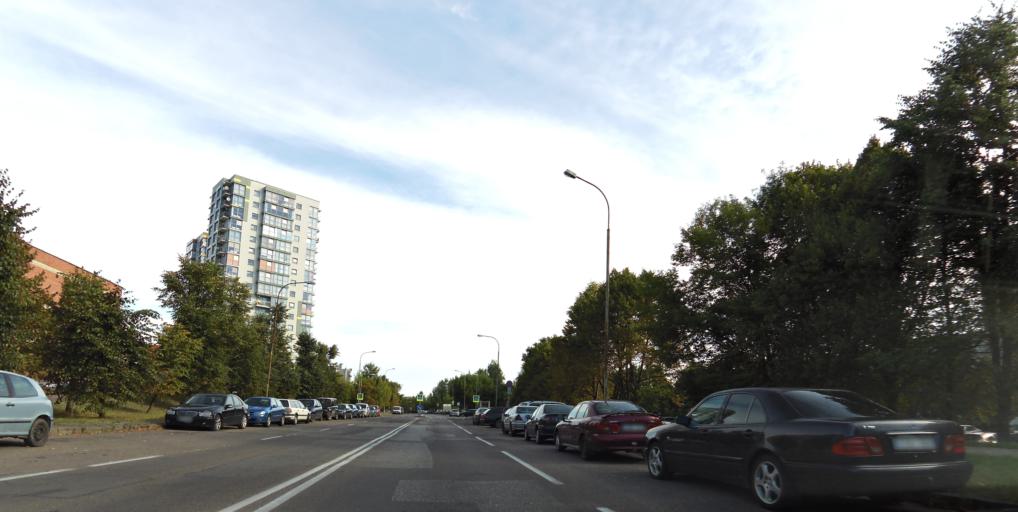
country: LT
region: Vilnius County
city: Seskine
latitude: 54.7121
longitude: 25.2511
